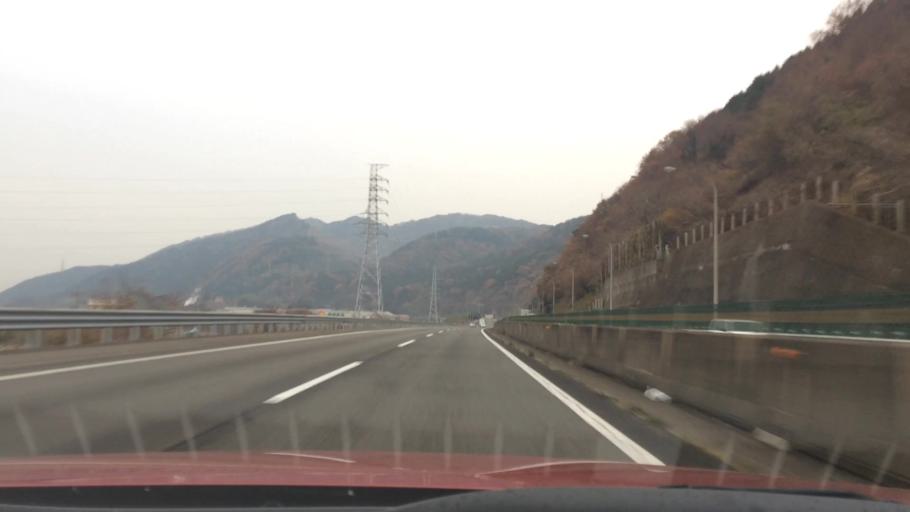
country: JP
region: Gifu
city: Tarui
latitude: 35.3267
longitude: 136.5354
